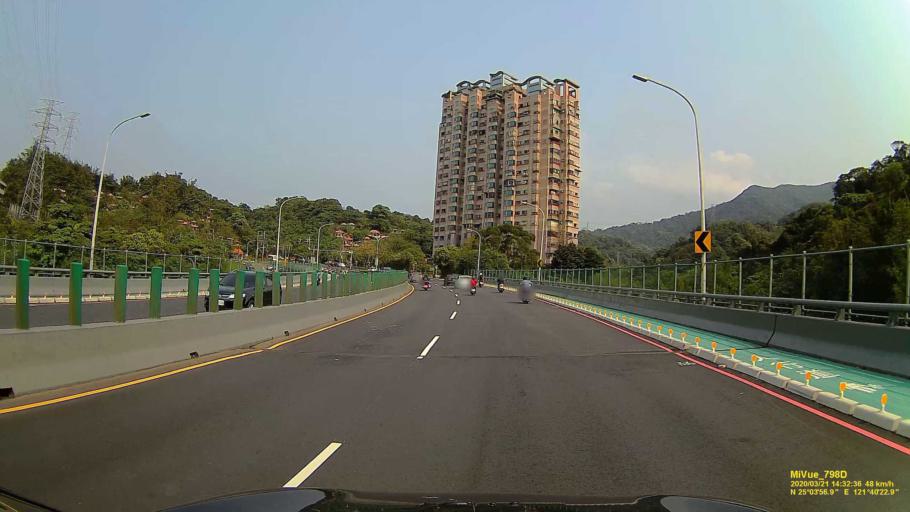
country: TW
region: Taiwan
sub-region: Keelung
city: Keelung
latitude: 25.0657
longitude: 121.6732
